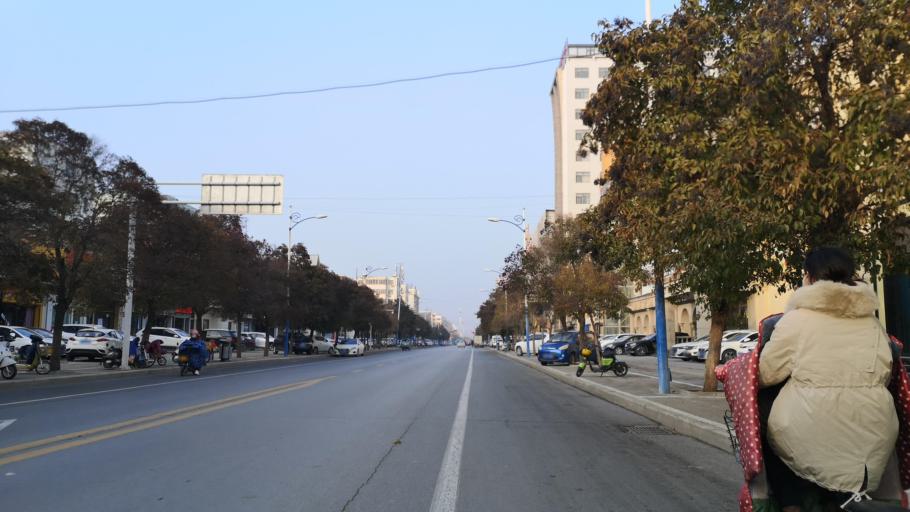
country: CN
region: Henan Sheng
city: Zhongyuanlu
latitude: 35.7669
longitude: 115.0632
